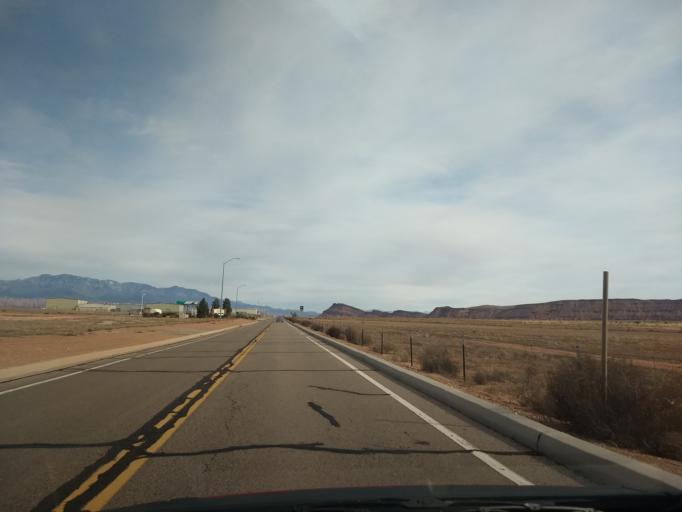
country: US
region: Utah
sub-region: Washington County
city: Washington
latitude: 37.0296
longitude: -113.5058
